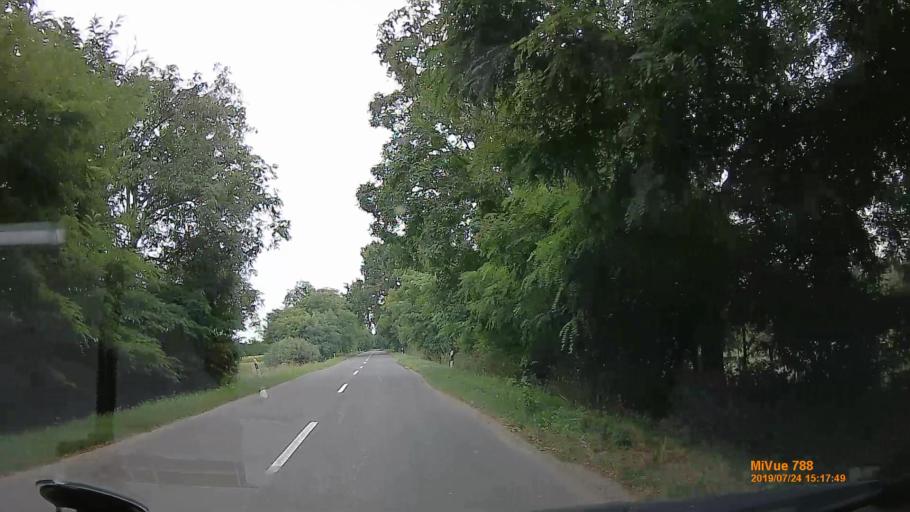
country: HU
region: Szabolcs-Szatmar-Bereg
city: Tarpa
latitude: 48.1881
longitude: 22.5484
